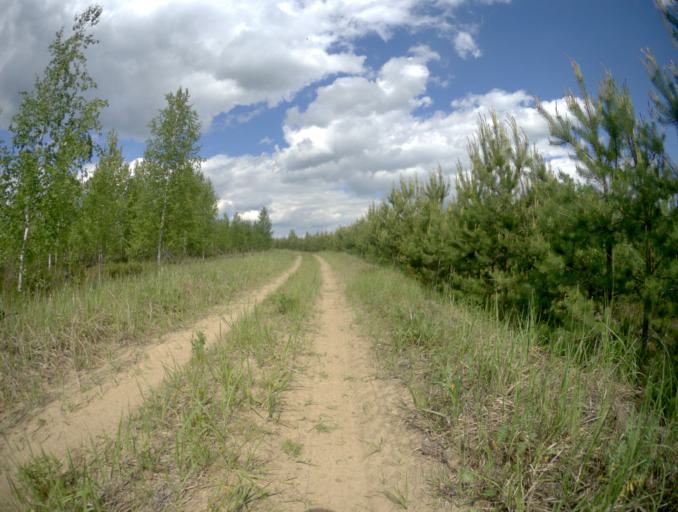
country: RU
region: Vladimir
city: Velikodvorskiy
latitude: 55.2715
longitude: 40.8639
